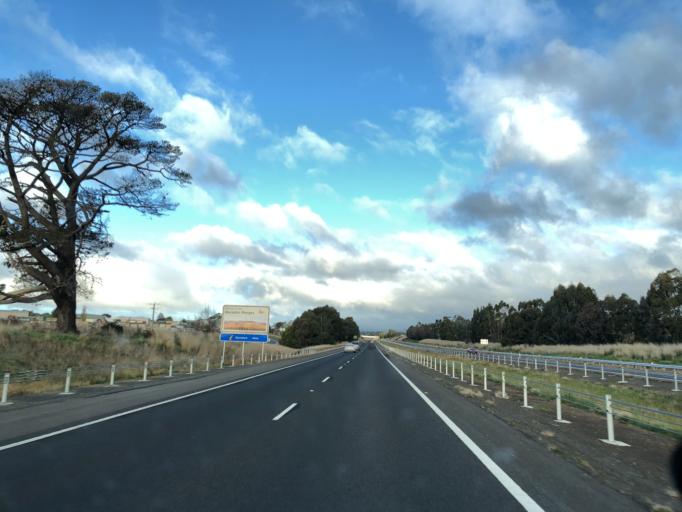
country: AU
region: Victoria
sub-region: Mount Alexander
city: Castlemaine
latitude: -37.2314
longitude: 144.4470
